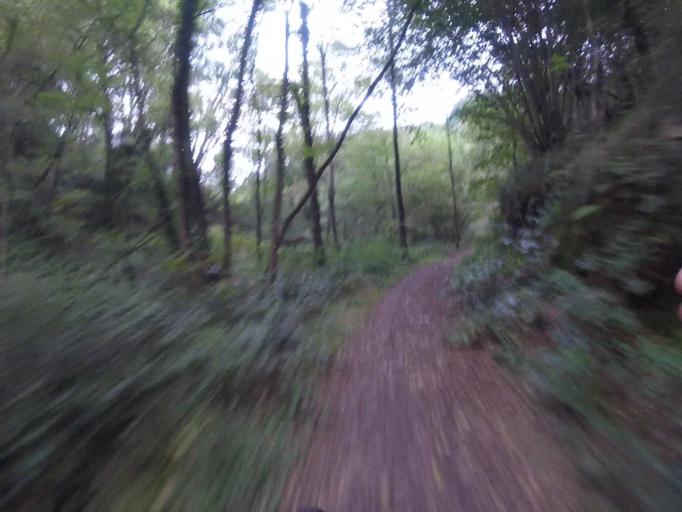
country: ES
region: Basque Country
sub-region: Provincia de Guipuzcoa
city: Errenteria
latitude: 43.2725
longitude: -1.8410
